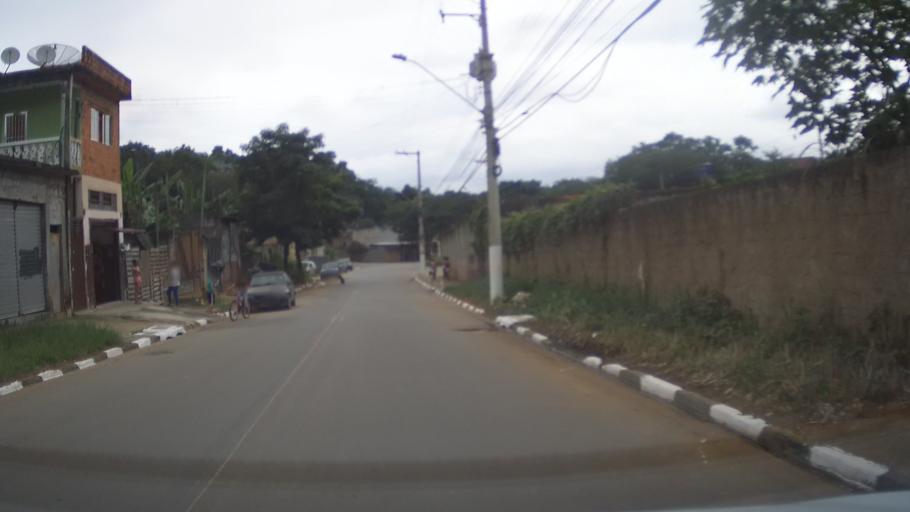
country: BR
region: Sao Paulo
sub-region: Aruja
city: Aruja
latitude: -23.3846
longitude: -46.3989
